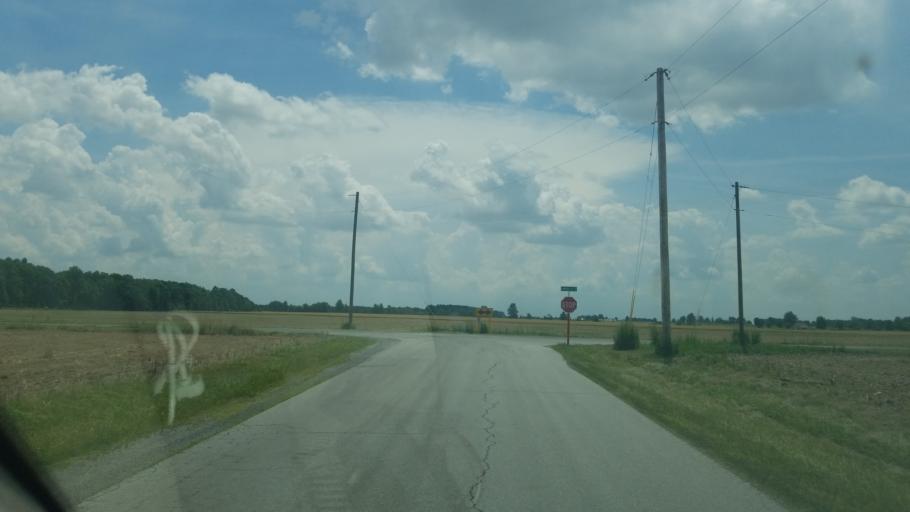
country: US
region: Ohio
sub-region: Hancock County
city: Arlington
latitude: 40.8195
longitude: -83.6001
